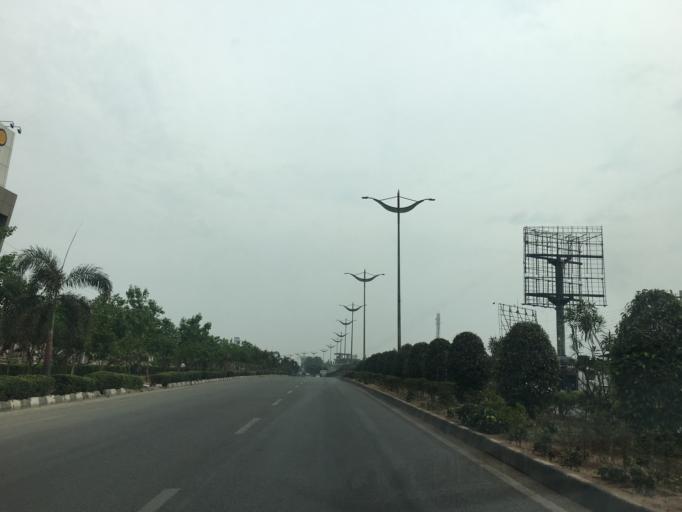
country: IN
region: Telangana
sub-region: Rangareddi
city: Balapur
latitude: 17.2967
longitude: 78.4184
